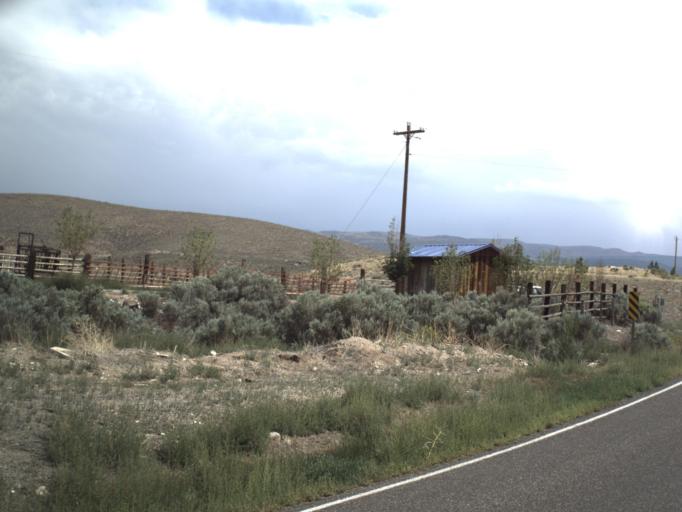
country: US
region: Utah
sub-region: Piute County
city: Junction
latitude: 38.1051
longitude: -111.9855
